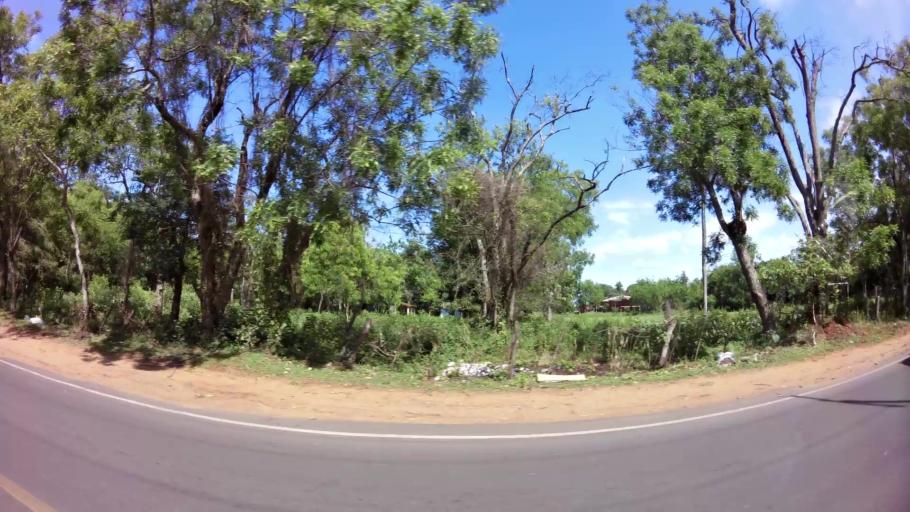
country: PY
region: Central
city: San Lorenzo
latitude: -25.2578
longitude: -57.4994
